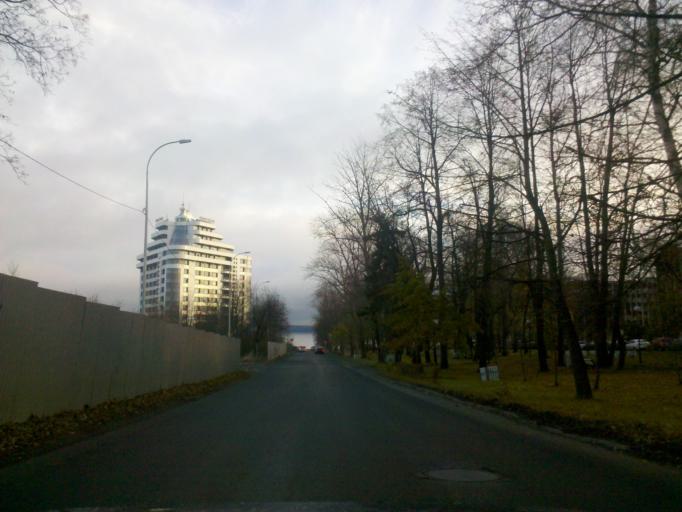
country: RU
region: Republic of Karelia
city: Petrozavodsk
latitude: 61.7938
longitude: 34.3684
